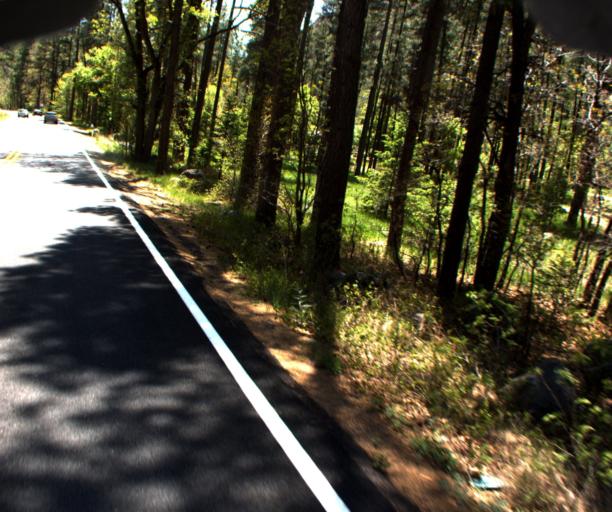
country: US
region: Arizona
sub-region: Coconino County
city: Kachina Village
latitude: 35.0113
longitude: -111.7381
